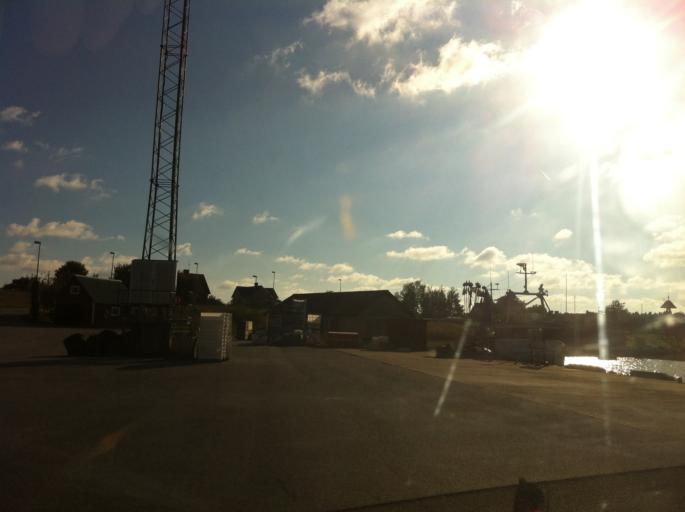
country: SE
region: Gotland
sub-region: Gotland
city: Slite
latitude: 57.4218
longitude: 18.9160
